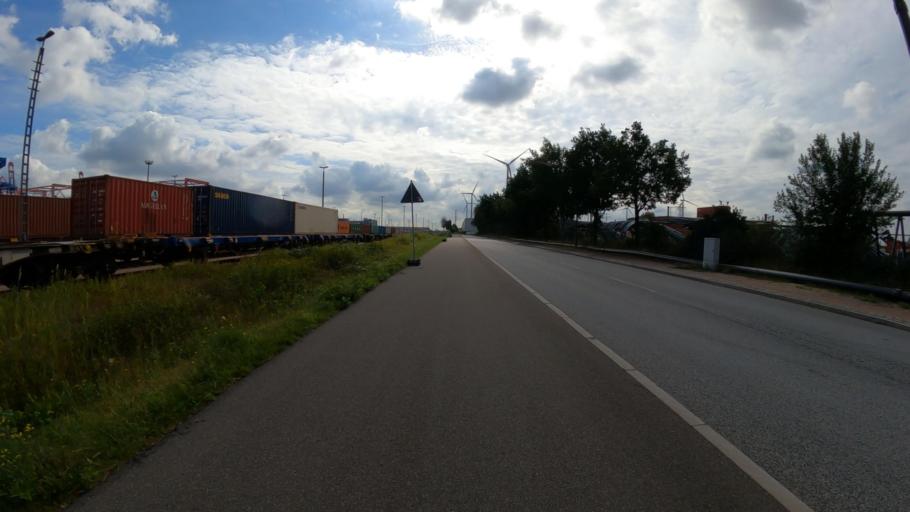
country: DE
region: Hamburg
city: Altona
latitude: 53.5297
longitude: 9.8973
